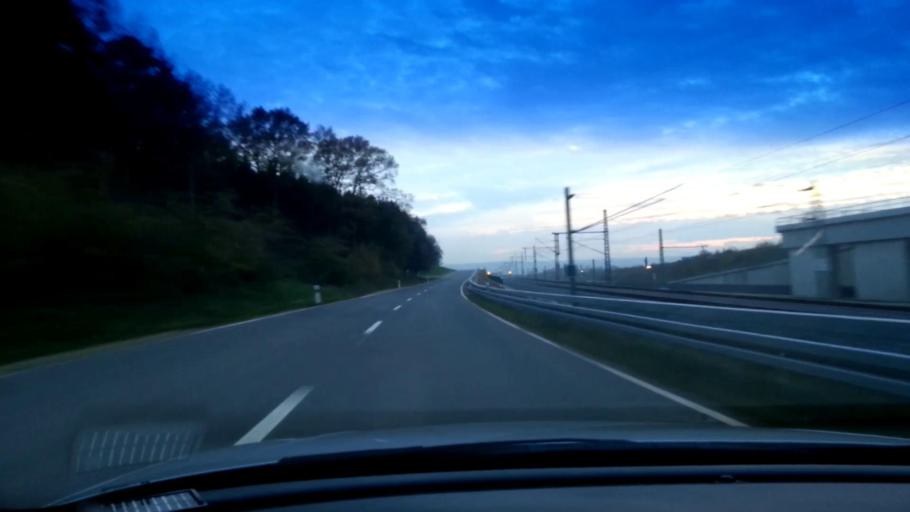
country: DE
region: Bavaria
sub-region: Upper Franconia
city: Breitengussbach
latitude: 49.9870
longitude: 10.9012
